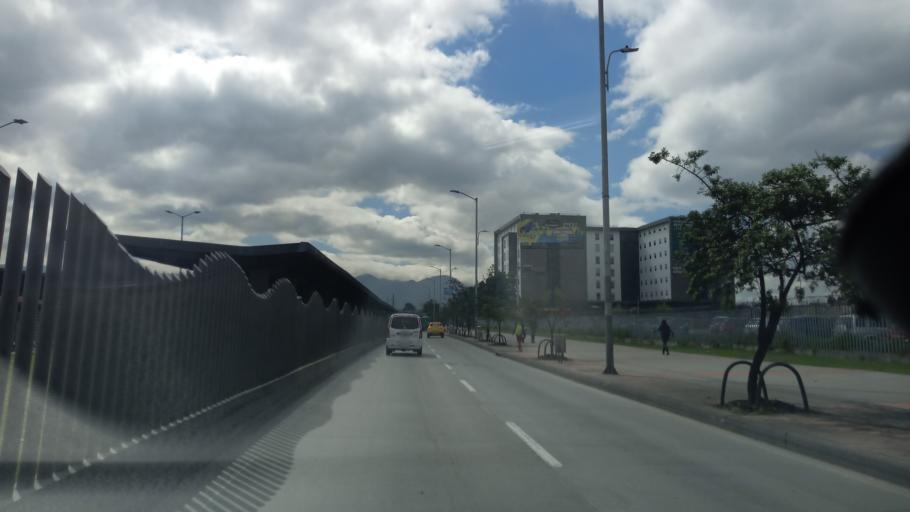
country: CO
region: Bogota D.C.
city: Bogota
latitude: 4.6826
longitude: -74.1226
